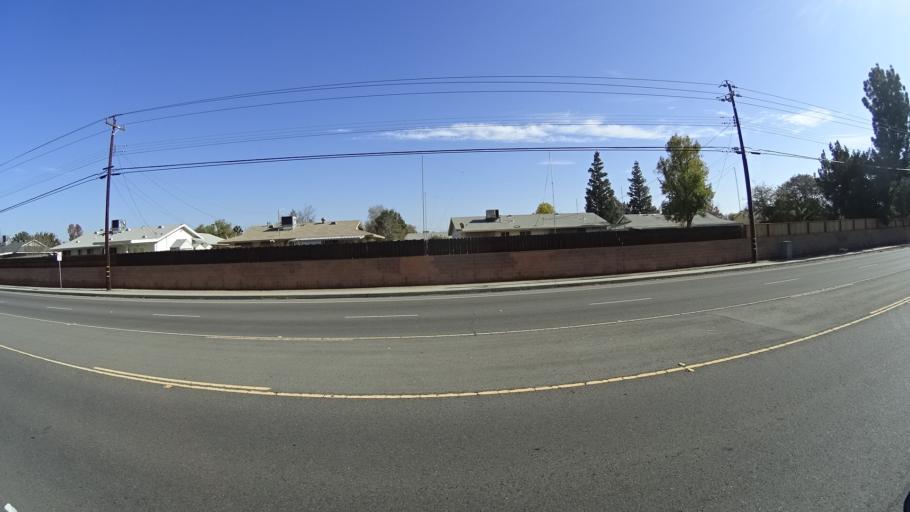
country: US
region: California
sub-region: Kern County
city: Greenacres
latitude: 35.3480
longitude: -119.0738
